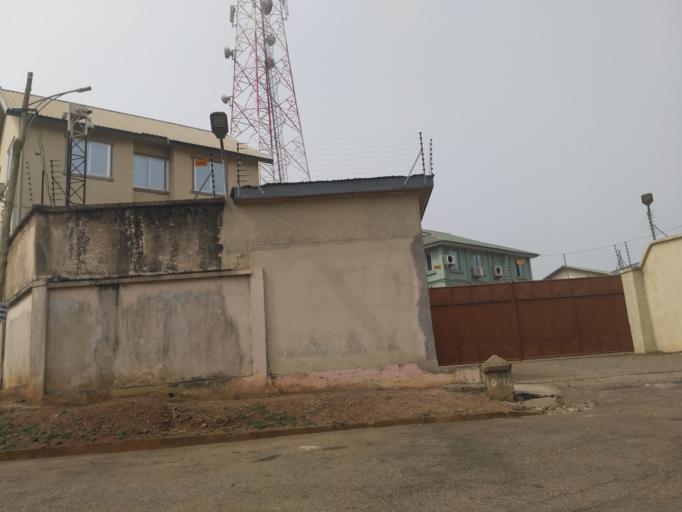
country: GH
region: Ashanti
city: Kumasi
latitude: 6.6843
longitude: -1.6271
